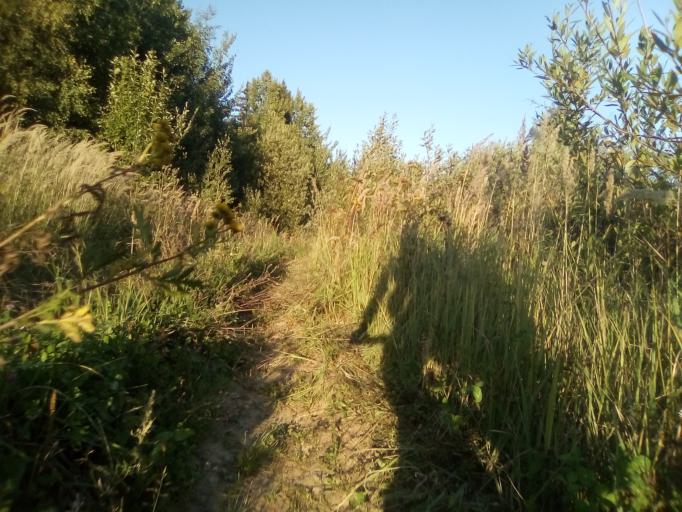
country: RU
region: Moskovskaya
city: Krasnoznamensk
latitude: 55.5812
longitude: 37.0507
